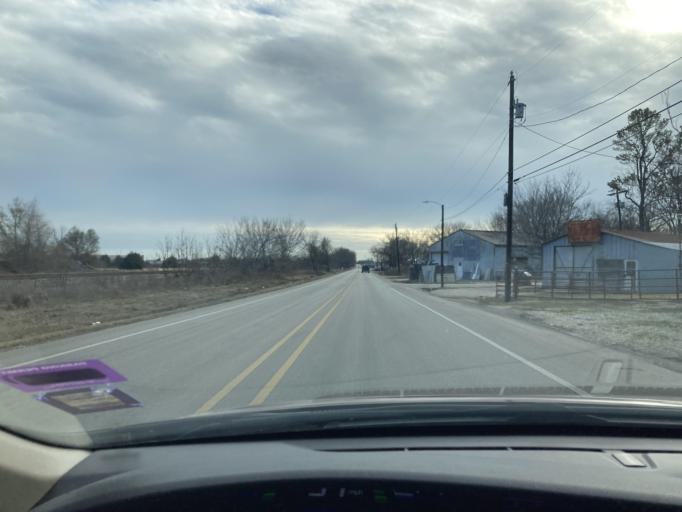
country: US
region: Texas
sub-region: Navarro County
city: Corsicana
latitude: 32.0813
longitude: -96.4629
